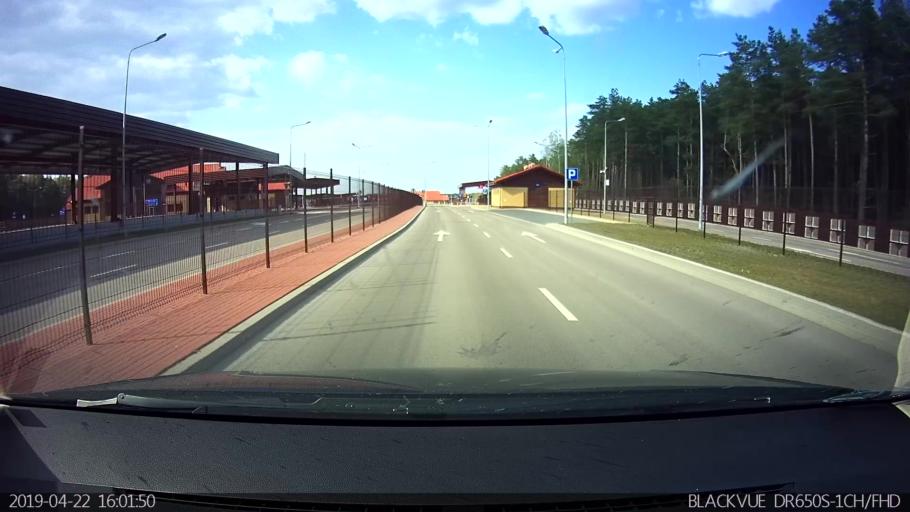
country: PL
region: Podlasie
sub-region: Powiat hajnowski
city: Czeremcha
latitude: 52.4723
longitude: 23.3578
